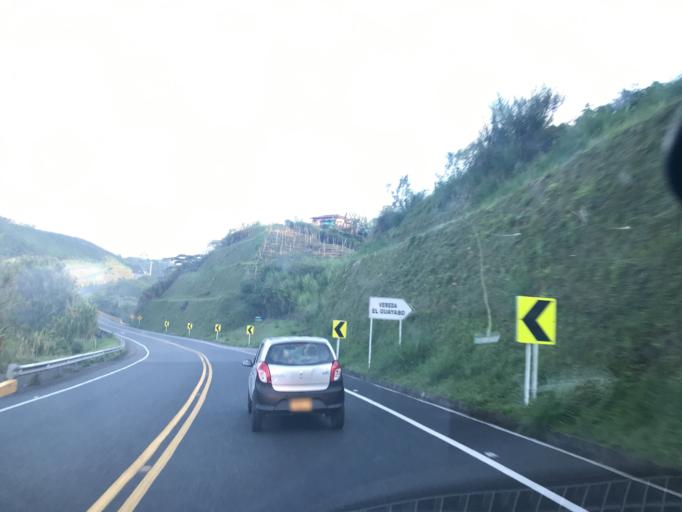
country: CO
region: Risaralda
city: Pereira
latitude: 4.7780
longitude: -75.7146
